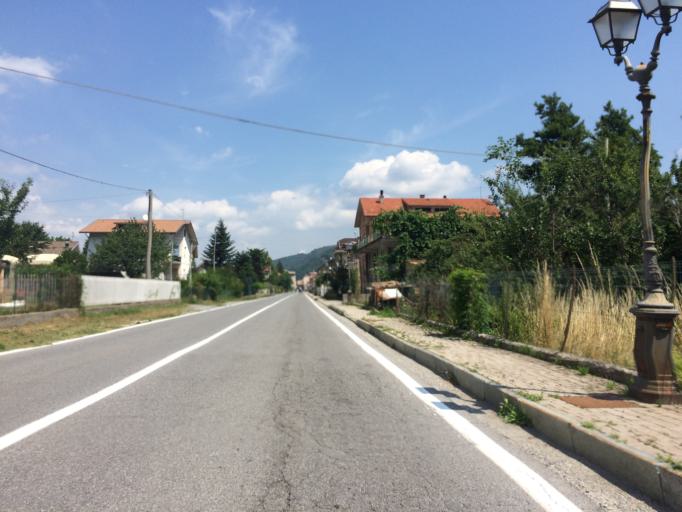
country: IT
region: Piedmont
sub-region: Provincia di Cuneo
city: Garessio
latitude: 44.1993
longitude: 8.0124
